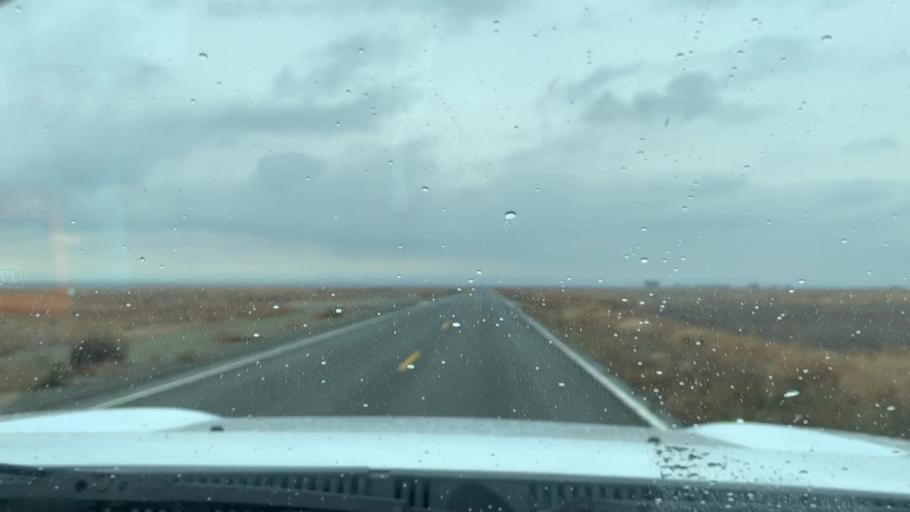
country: US
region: California
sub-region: Kings County
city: Kettleman City
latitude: 35.9341
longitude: -119.7890
